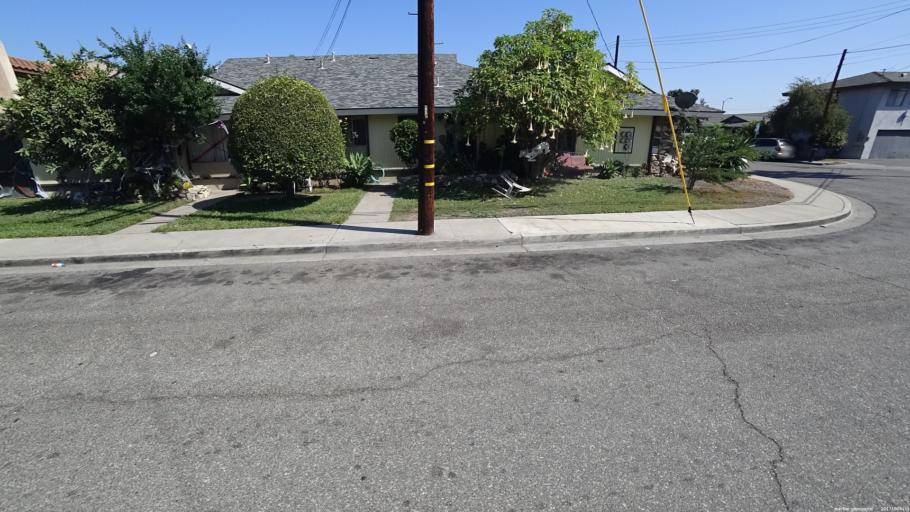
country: US
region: California
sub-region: Orange County
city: Garden Grove
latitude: 33.7709
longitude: -117.9453
